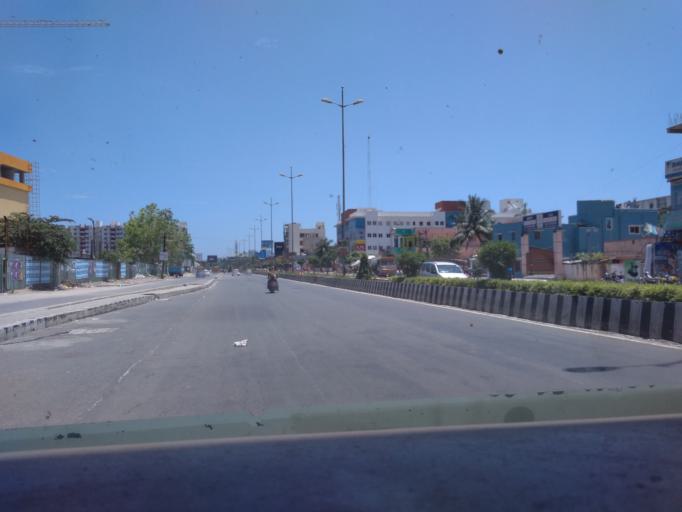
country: IN
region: Tamil Nadu
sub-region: Kancheepuram
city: Injambakkam
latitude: 12.8368
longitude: 80.2284
